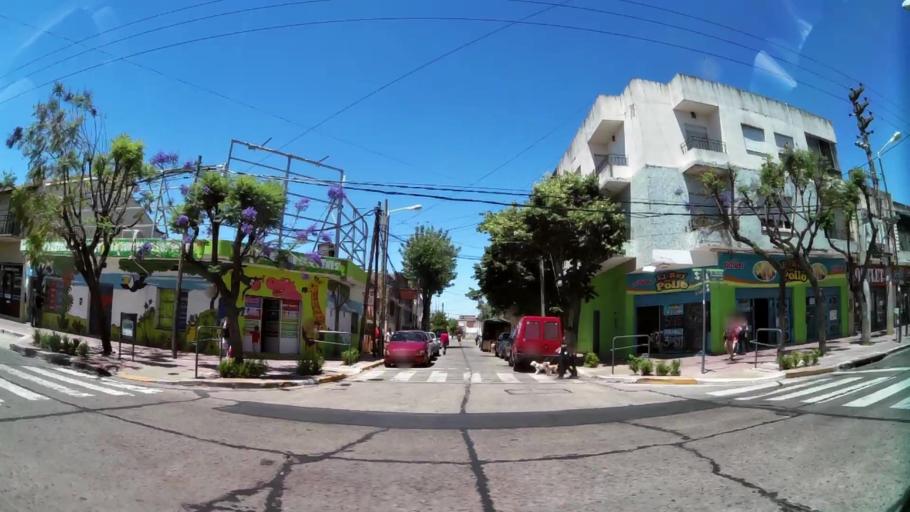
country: AR
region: Buenos Aires
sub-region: Partido de Tigre
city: Tigre
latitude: -34.4541
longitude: -58.5587
